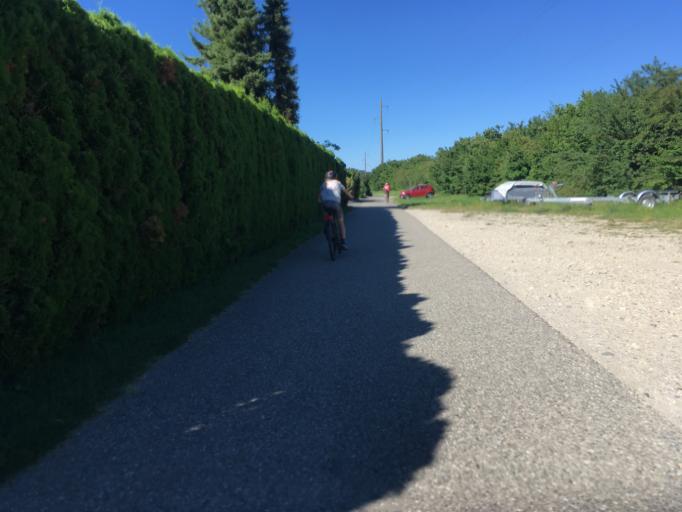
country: CH
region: Vaud
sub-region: Broye-Vully District
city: Avenches
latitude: 46.9153
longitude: 7.0258
